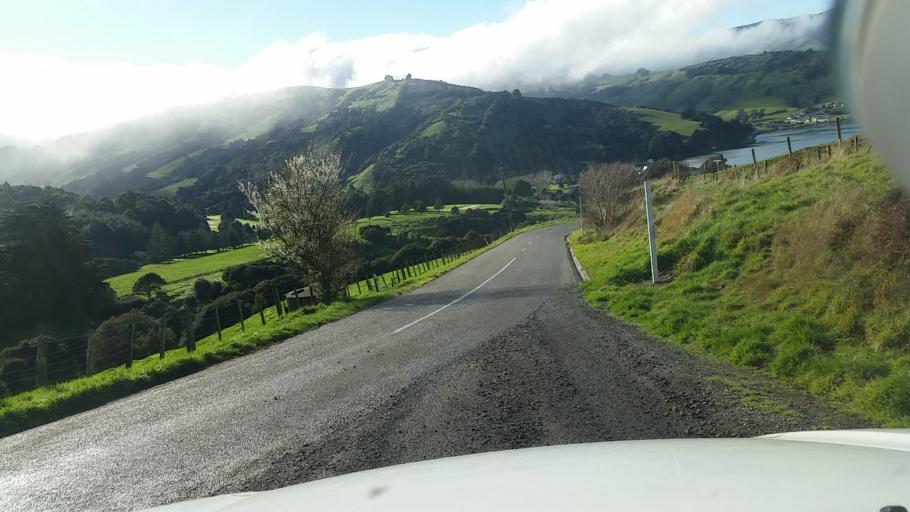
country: NZ
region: Canterbury
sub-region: Christchurch City
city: Christchurch
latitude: -43.7500
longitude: 172.9177
